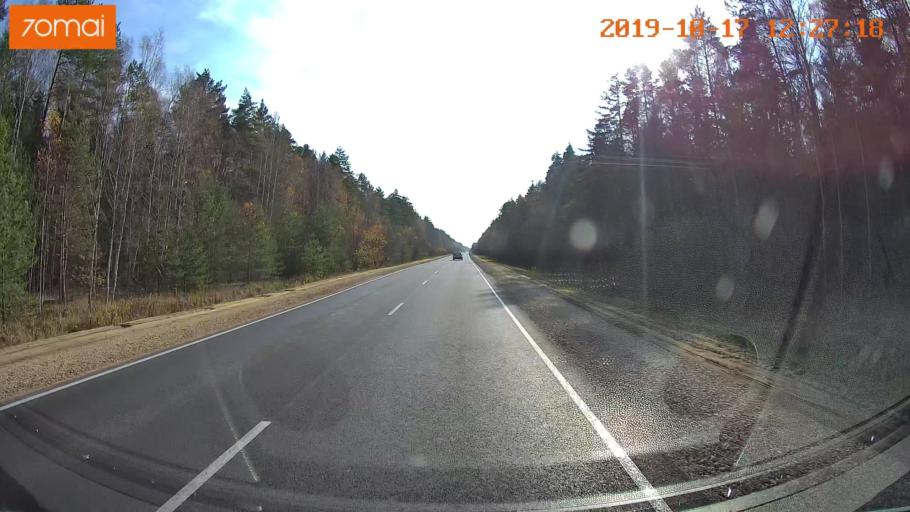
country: RU
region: Rjazan
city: Syntul
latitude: 55.0066
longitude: 41.2618
